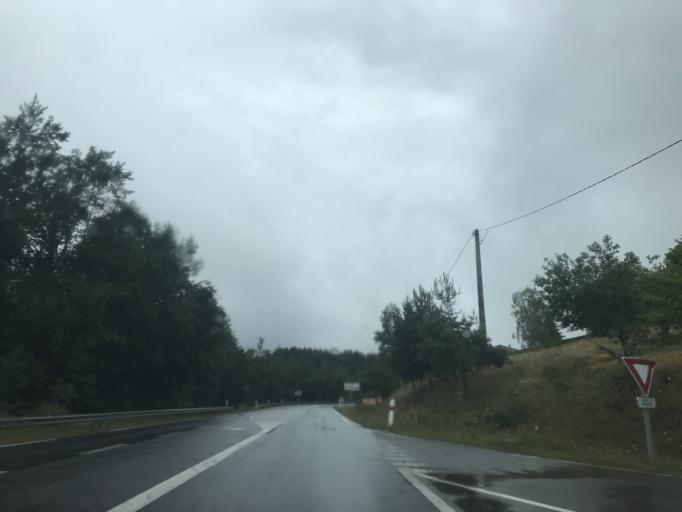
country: FR
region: Auvergne
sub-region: Departement du Puy-de-Dome
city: Job
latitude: 45.6284
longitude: 3.7139
